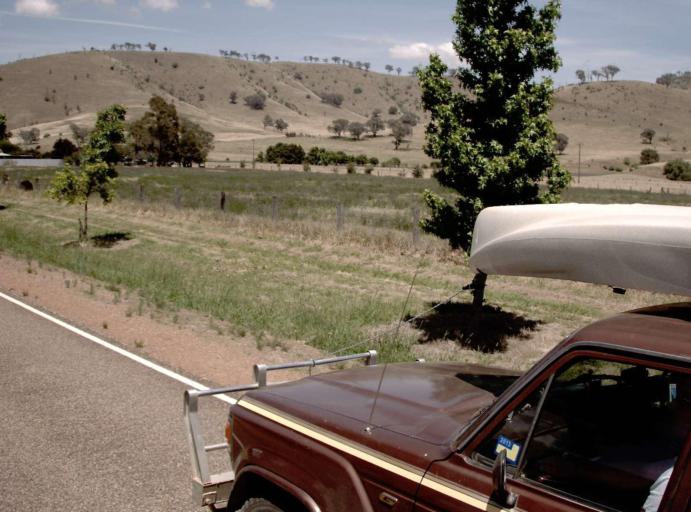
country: AU
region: Victoria
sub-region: East Gippsland
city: Bairnsdale
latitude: -37.2473
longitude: 147.7125
